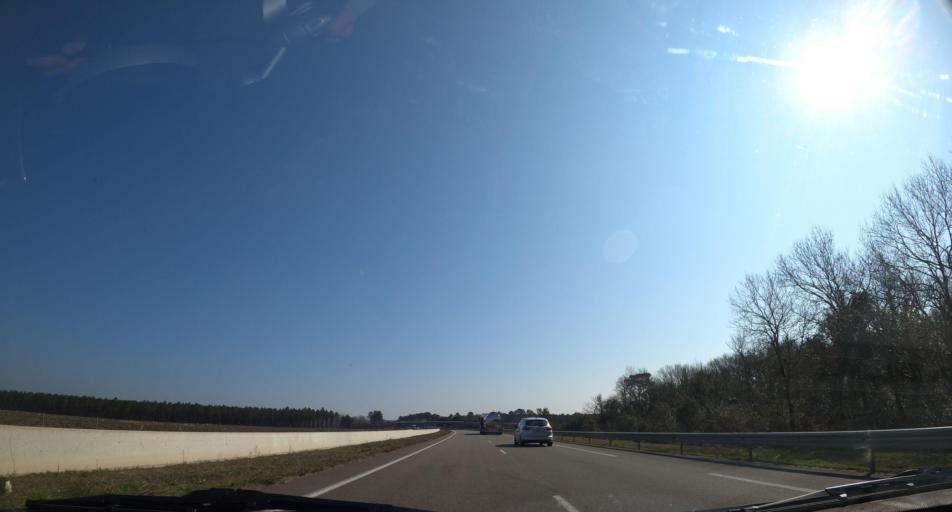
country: FR
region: Aquitaine
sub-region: Departement des Landes
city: Saint-Geours-de-Maremne
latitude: 43.6947
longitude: -1.2112
